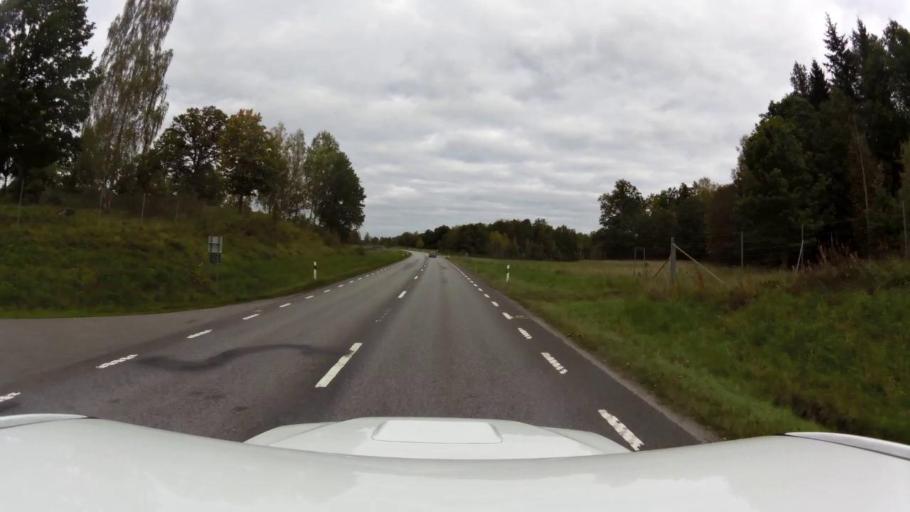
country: SE
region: OEstergoetland
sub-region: Kinda Kommun
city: Rimforsa
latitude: 58.2183
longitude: 15.6645
